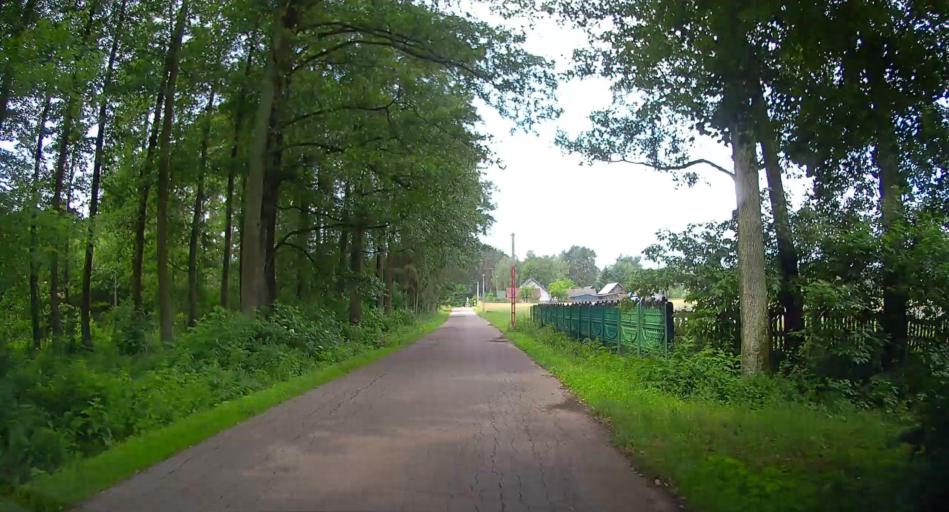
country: PL
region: Masovian Voivodeship
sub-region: Powiat ostrowski
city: Brok
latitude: 52.7424
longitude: 21.7290
